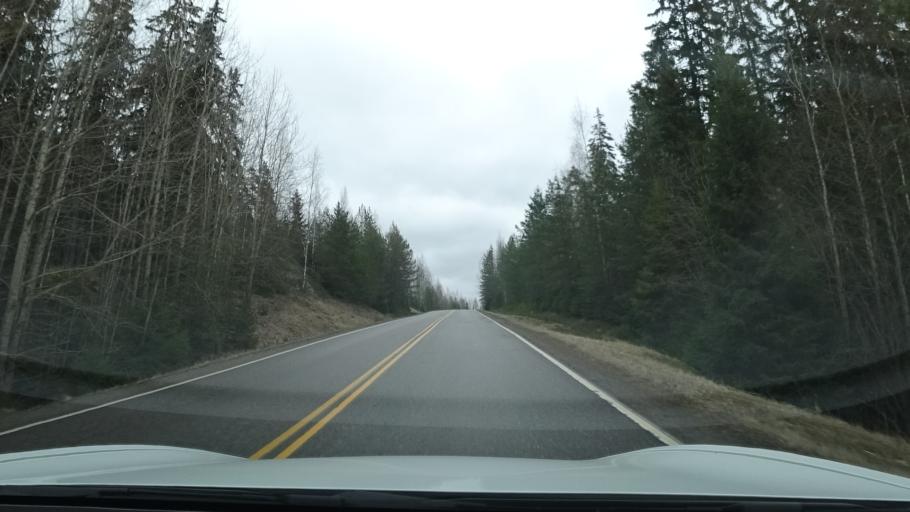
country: FI
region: Uusimaa
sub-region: Helsinki
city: Pornainen
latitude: 60.4841
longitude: 25.4007
